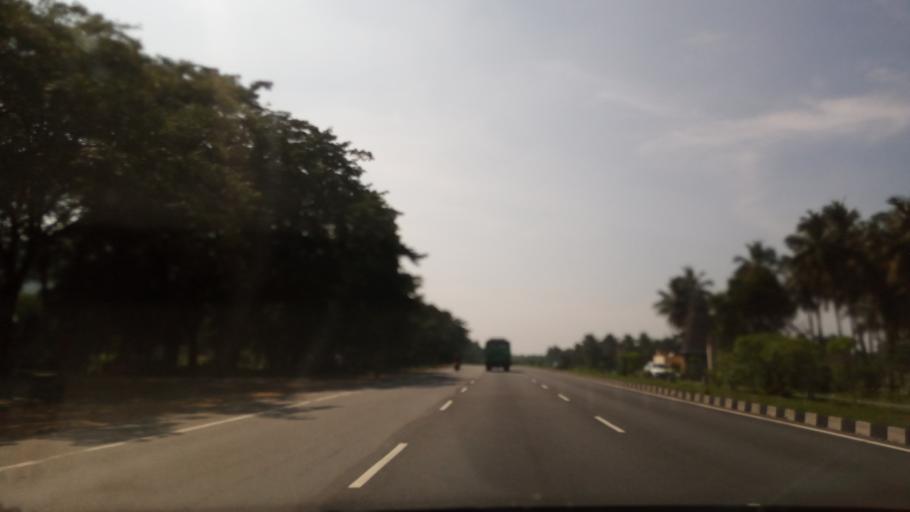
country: IN
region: Tamil Nadu
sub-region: Vellore
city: Gudiyatham
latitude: 12.8879
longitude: 78.8808
